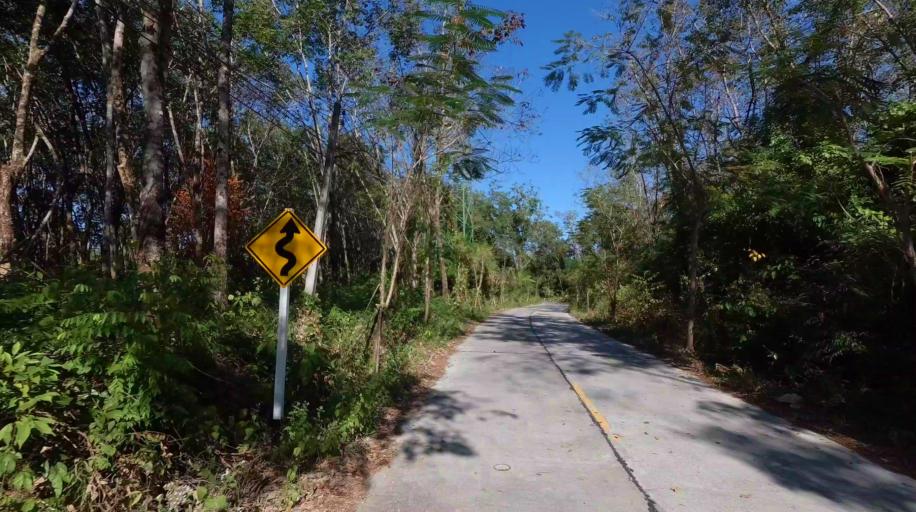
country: TH
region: Trat
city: Ko Kut
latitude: 11.6142
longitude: 102.5430
